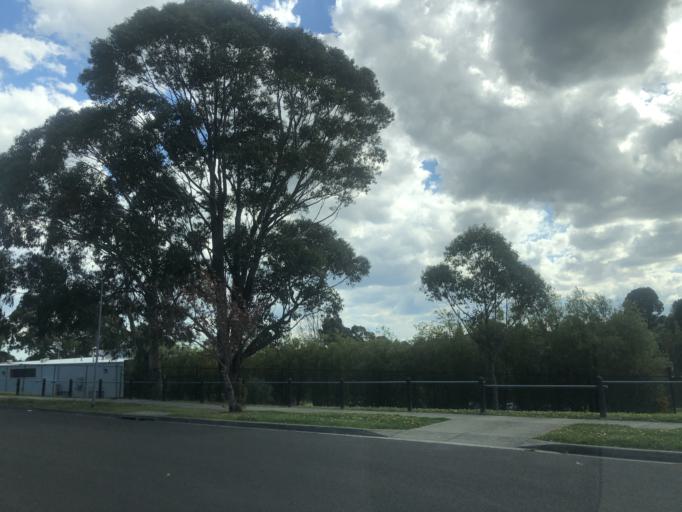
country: AU
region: Victoria
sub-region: Casey
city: Endeavour Hills
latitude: -37.9866
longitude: 145.2619
